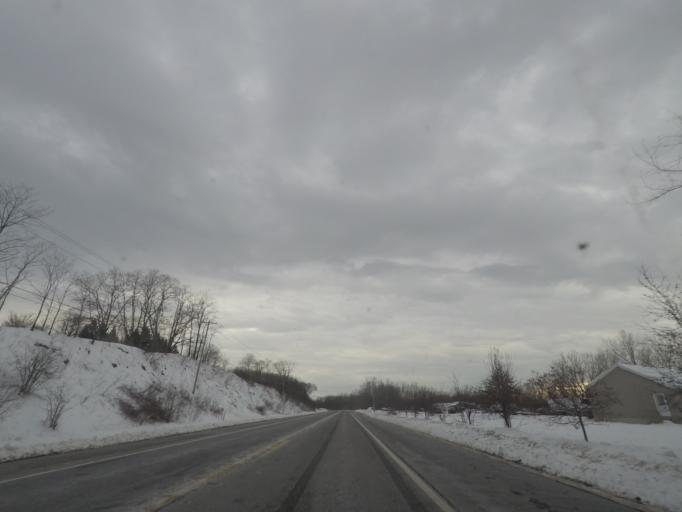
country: US
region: New York
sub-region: Rensselaer County
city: Hampton Manor
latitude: 42.6082
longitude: -73.7478
